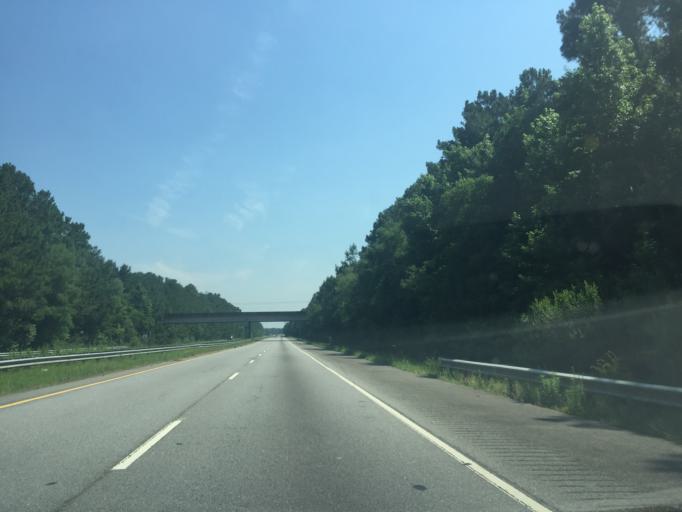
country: US
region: Georgia
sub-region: Chatham County
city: Georgetown
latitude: 32.0264
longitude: -81.1700
